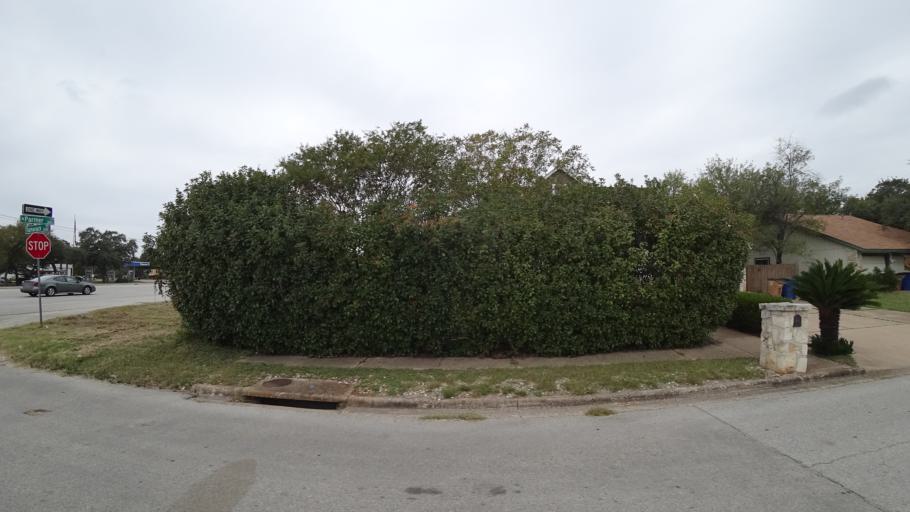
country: US
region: Texas
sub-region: Travis County
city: Wells Branch
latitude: 30.4246
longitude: -97.7121
